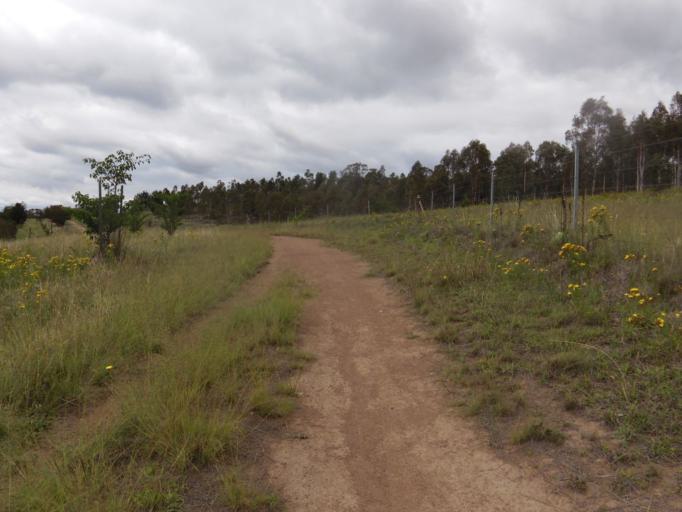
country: AU
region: Australian Capital Territory
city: Macquarie
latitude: -35.3375
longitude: 149.0260
